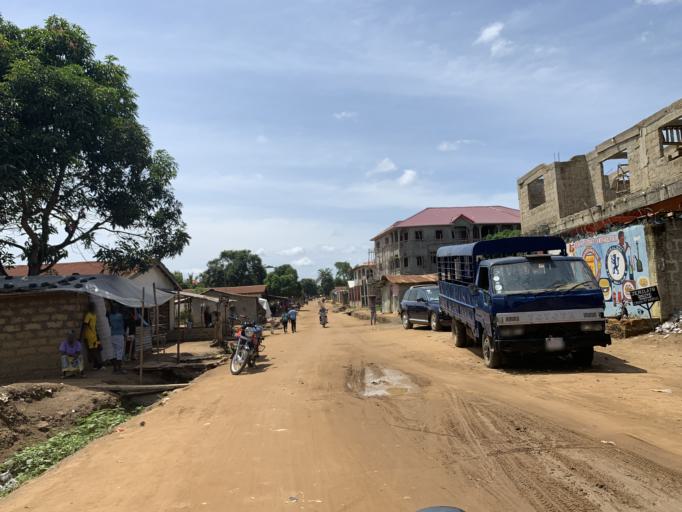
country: SL
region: Western Area
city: Waterloo
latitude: 8.3365
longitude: -13.0491
